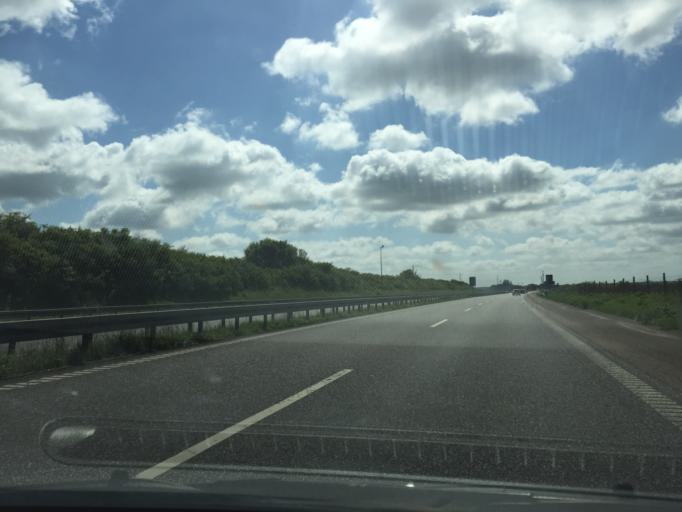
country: DK
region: Zealand
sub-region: Guldborgsund Kommune
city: Sundby
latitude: 54.8422
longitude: 11.8220
